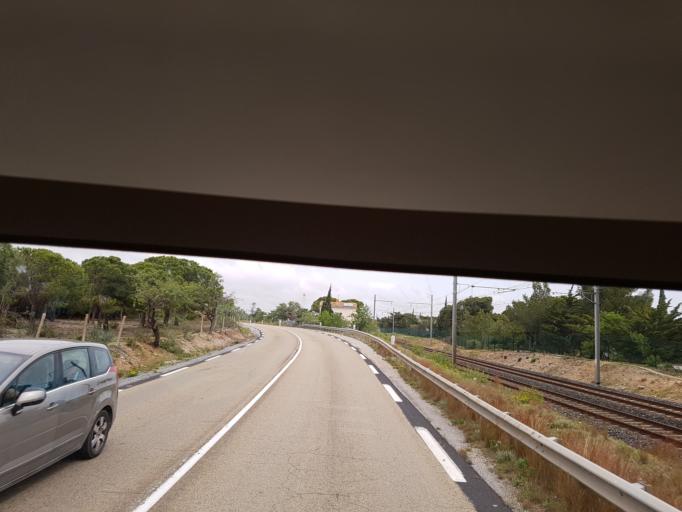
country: FR
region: Languedoc-Roussillon
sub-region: Departement de l'Aude
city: Leucate
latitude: 42.8771
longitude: 2.9931
